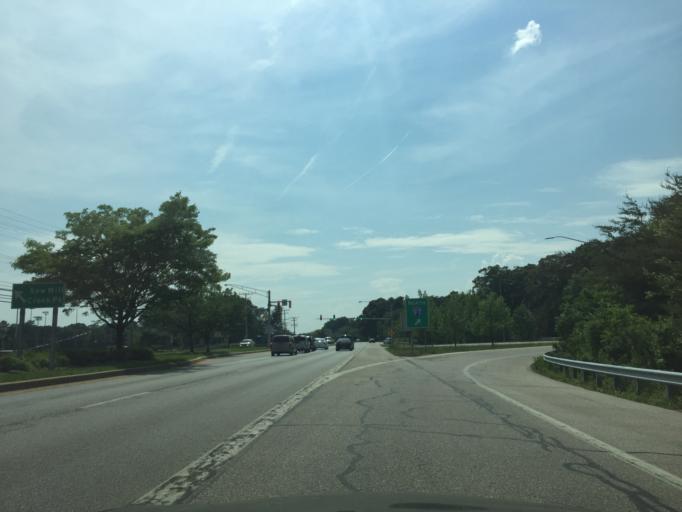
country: US
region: Maryland
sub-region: Anne Arundel County
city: Glen Burnie
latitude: 39.1680
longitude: -76.6375
